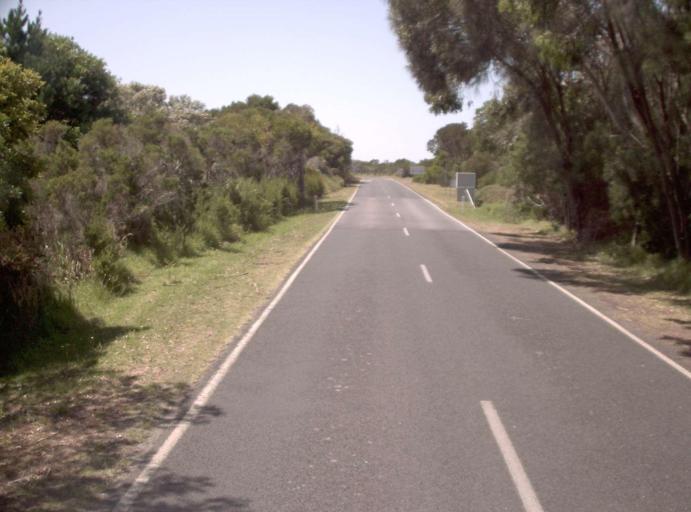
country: AU
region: Victoria
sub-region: Bass Coast
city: North Wonthaggi
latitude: -38.6692
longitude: 145.6220
